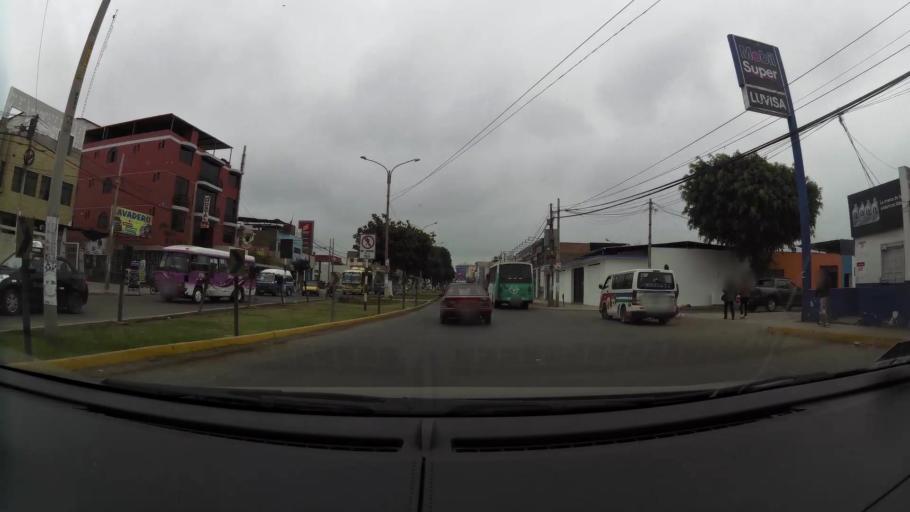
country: PE
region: La Libertad
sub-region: Provincia de Trujillo
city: Trujillo
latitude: -8.1217
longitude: -79.0211
